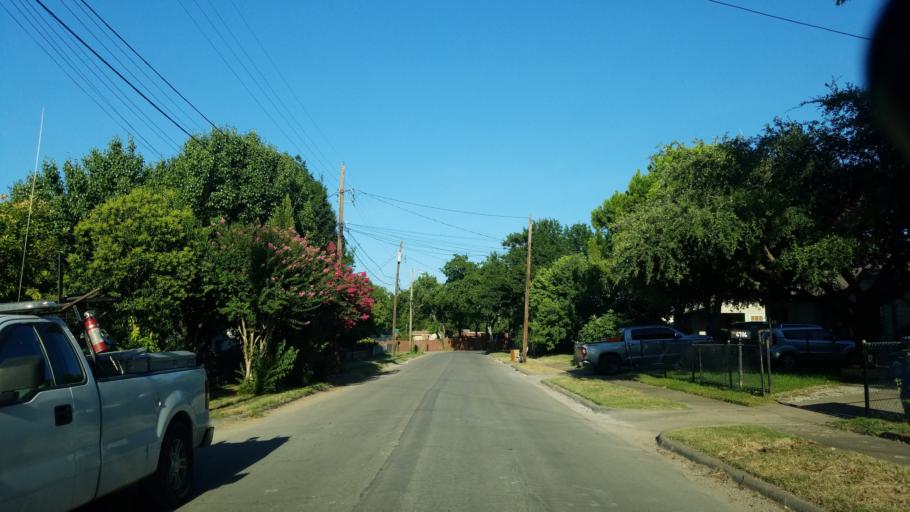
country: US
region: Texas
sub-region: Dallas County
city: Balch Springs
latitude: 32.7765
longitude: -96.7037
